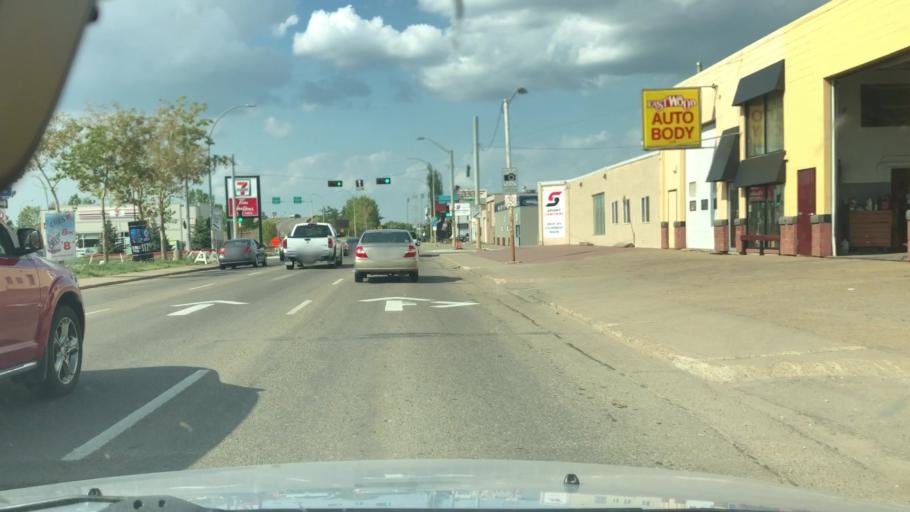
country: CA
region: Alberta
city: Edmonton
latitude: 53.5714
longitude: -113.4521
